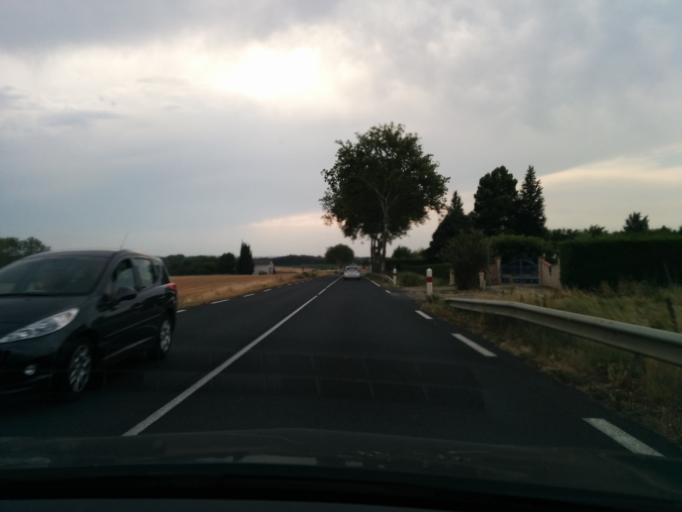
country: FR
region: Languedoc-Roussillon
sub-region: Departement de l'Aude
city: Saint-Martin-Lalande
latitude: 43.2939
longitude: 2.0207
